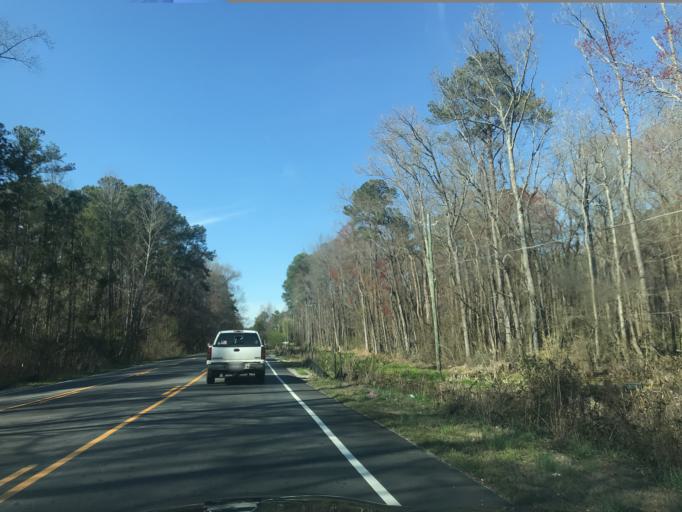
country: US
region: North Carolina
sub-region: Wake County
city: Fuquay-Varina
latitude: 35.5841
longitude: -78.7569
